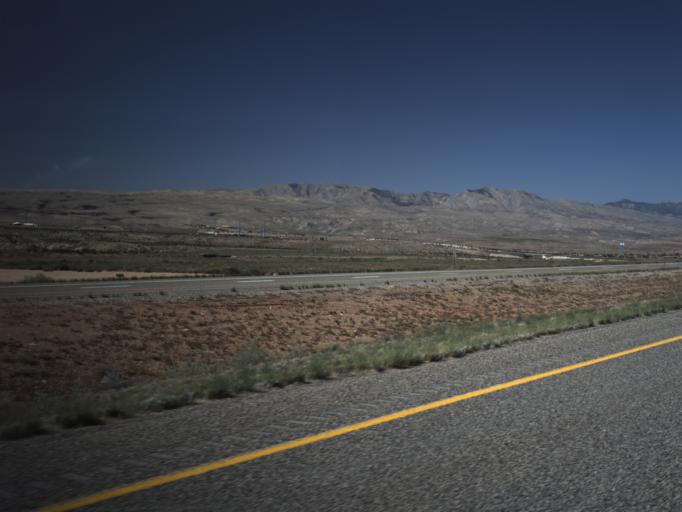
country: US
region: Utah
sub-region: Washington County
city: Saint George
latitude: 37.0163
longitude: -113.5949
